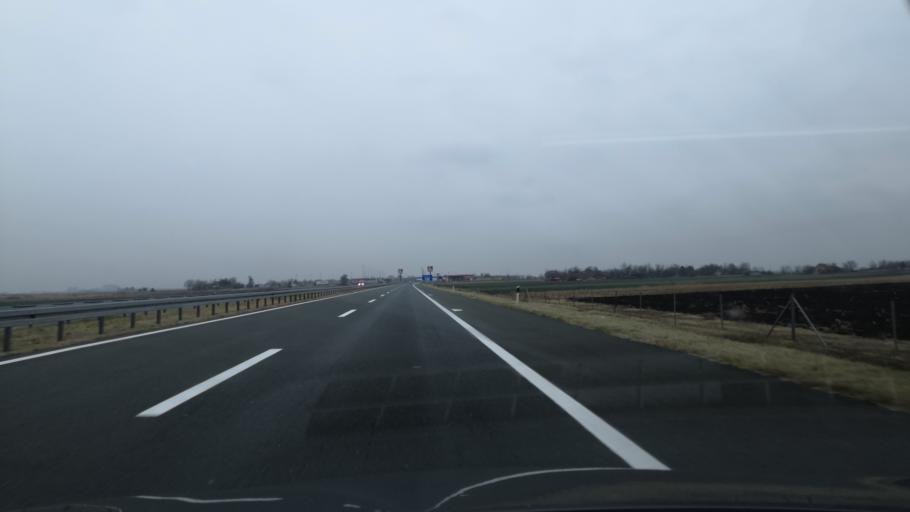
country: RS
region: Autonomna Pokrajina Vojvodina
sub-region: Severnobacki Okrug
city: Subotica
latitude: 45.9611
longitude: 19.7113
